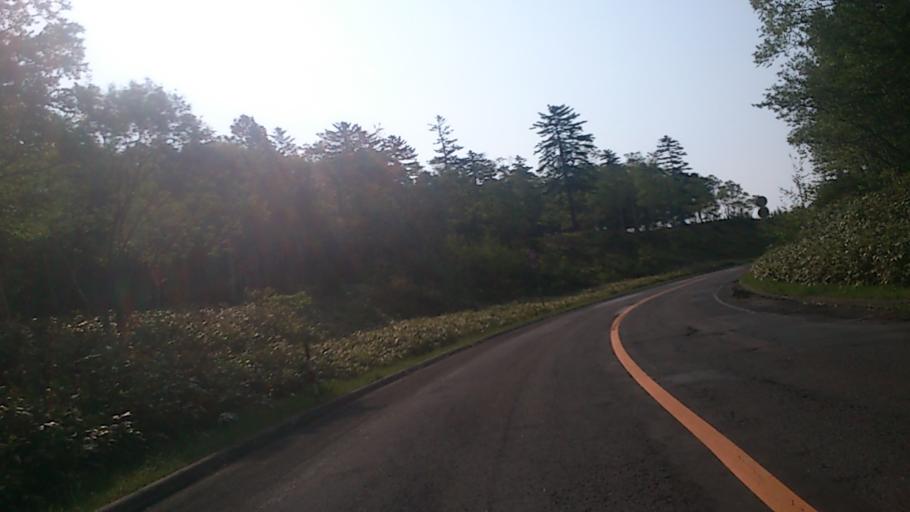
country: JP
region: Hokkaido
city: Bihoro
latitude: 43.4450
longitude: 144.1877
